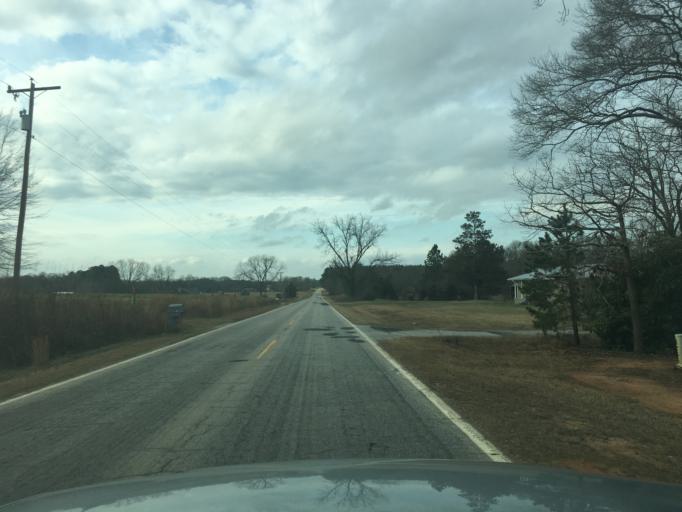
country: US
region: South Carolina
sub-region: Abbeville County
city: Due West
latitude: 34.3295
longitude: -82.4783
